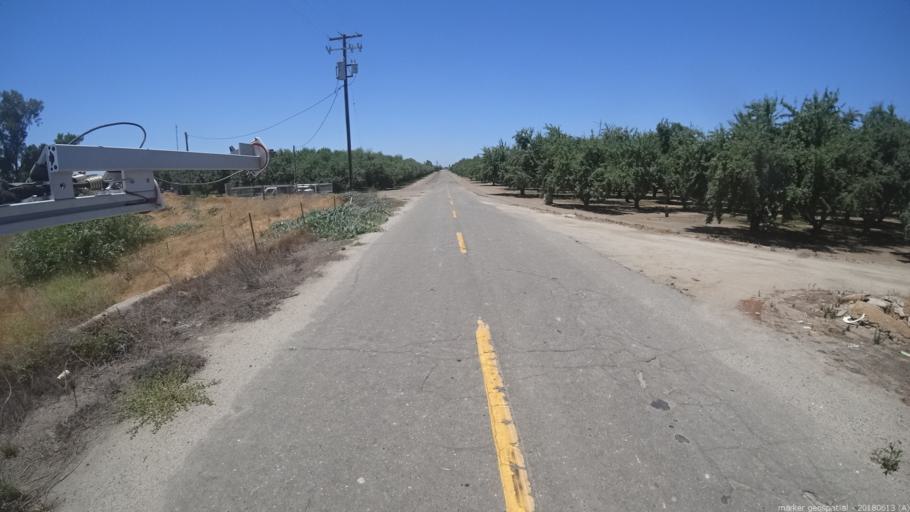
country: US
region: California
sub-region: Madera County
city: Chowchilla
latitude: 37.0618
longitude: -120.2793
